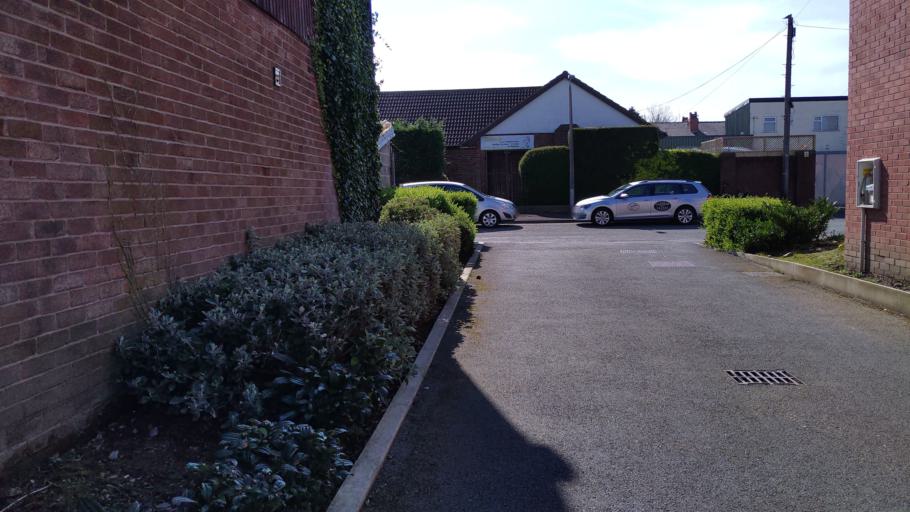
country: GB
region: England
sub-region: Lancashire
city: Chorley
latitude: 53.6469
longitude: -2.6360
